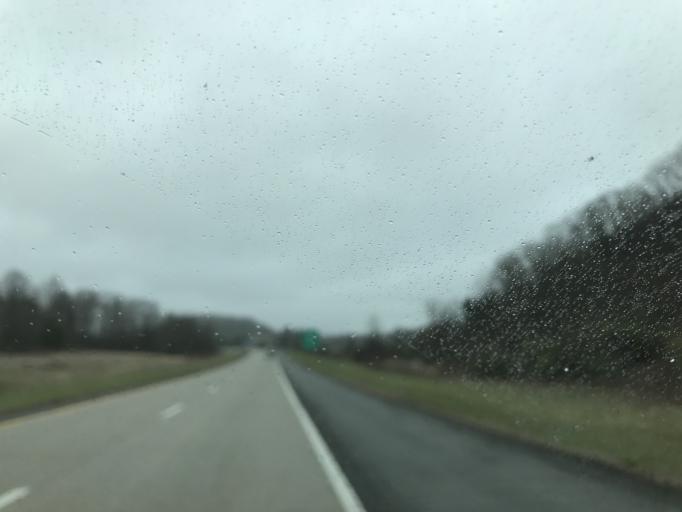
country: US
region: West Virginia
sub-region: Greenbrier County
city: Rainelle
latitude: 37.8419
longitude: -80.7387
